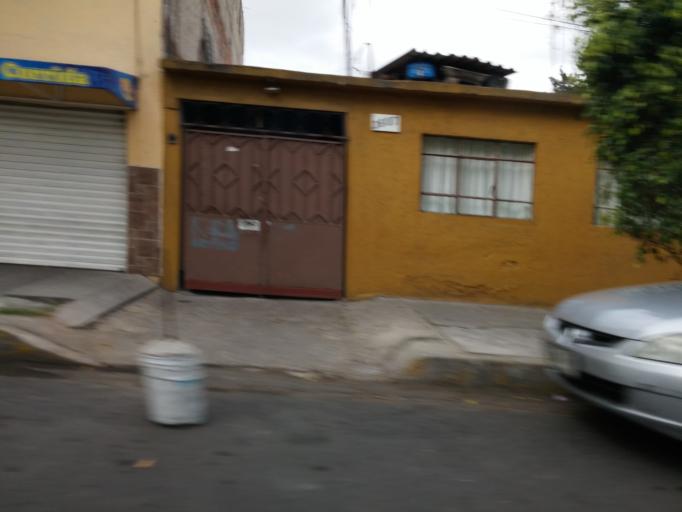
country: MX
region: Mexico City
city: Azcapotzalco
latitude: 19.4615
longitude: -99.1749
